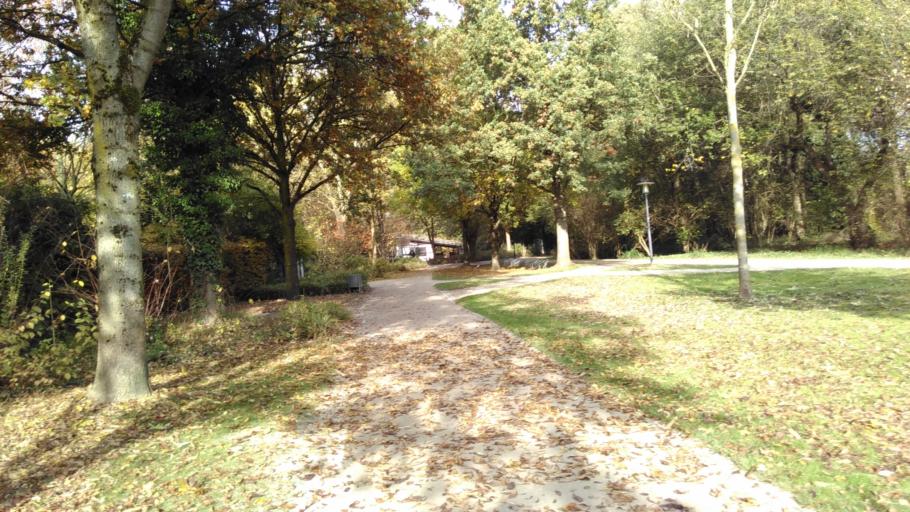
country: DE
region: North Rhine-Westphalia
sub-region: Regierungsbezirk Detmold
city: Rheda-Wiedenbruck
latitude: 51.8454
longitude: 8.3007
